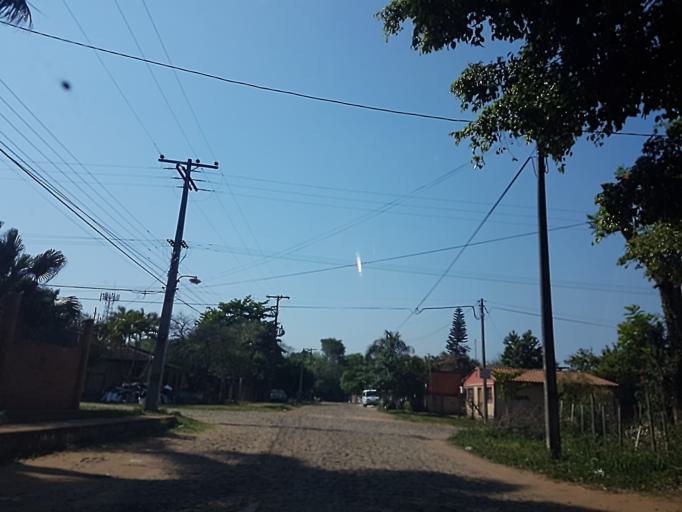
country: PY
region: Central
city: Colonia Mariano Roque Alonso
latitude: -25.2148
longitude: -57.5213
